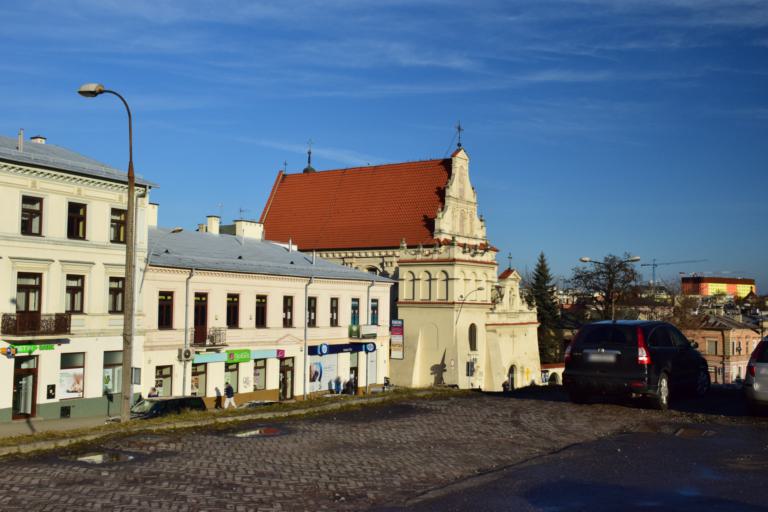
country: PL
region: Lublin Voivodeship
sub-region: Powiat lubelski
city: Lublin
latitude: 51.2486
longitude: 22.5652
